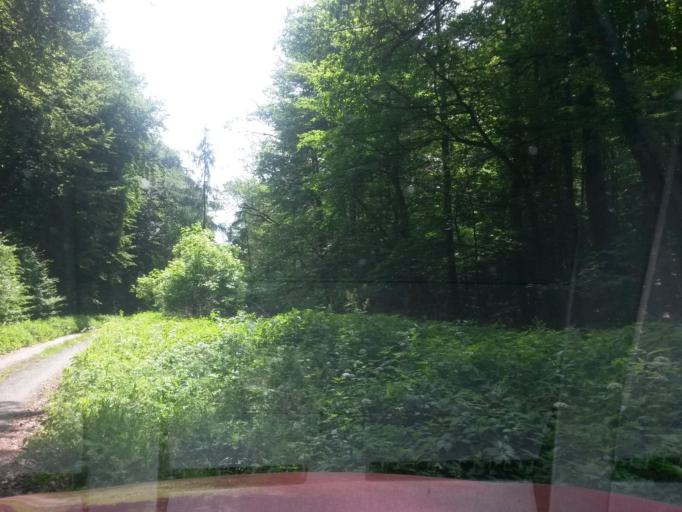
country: SK
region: Kosicky
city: Kosice
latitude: 48.7386
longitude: 21.1132
